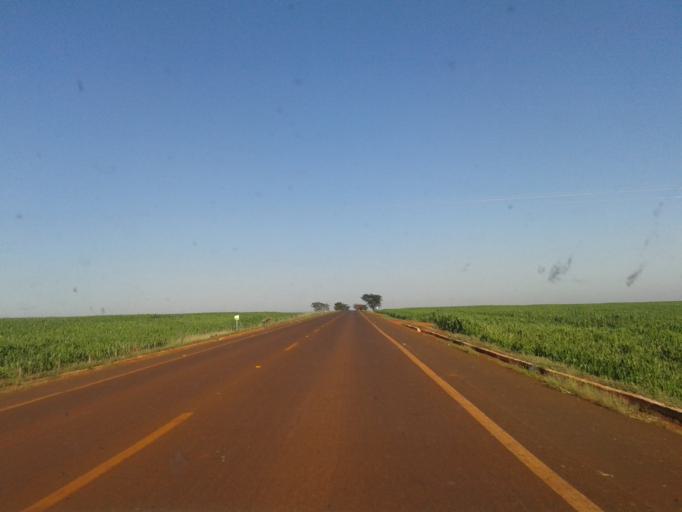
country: BR
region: Minas Gerais
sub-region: Capinopolis
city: Capinopolis
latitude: -18.6978
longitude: -49.6380
